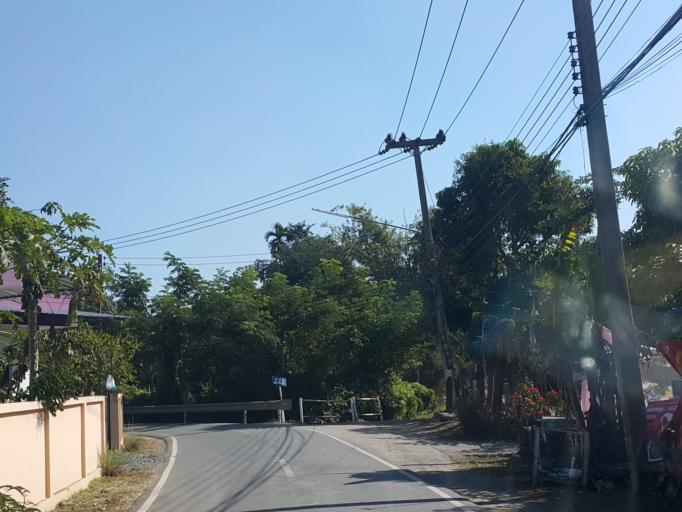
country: TH
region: Chiang Mai
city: San Sai
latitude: 18.8764
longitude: 99.0017
